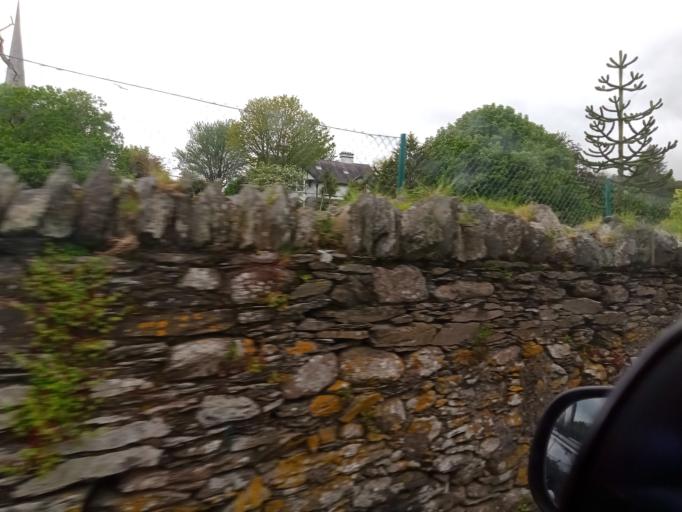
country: IE
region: Munster
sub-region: County Cork
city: Derry
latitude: 51.5784
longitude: -9.0285
